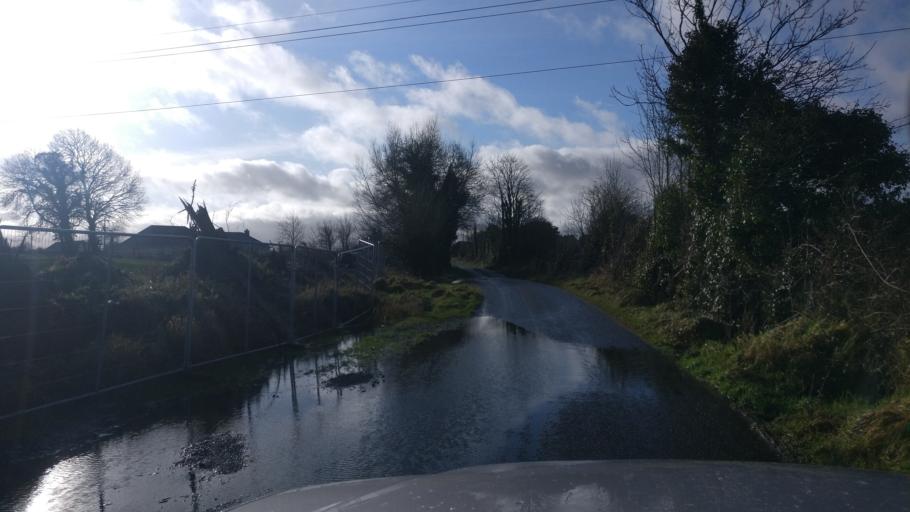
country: IE
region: Connaught
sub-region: County Galway
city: Loughrea
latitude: 53.2530
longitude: -8.6046
